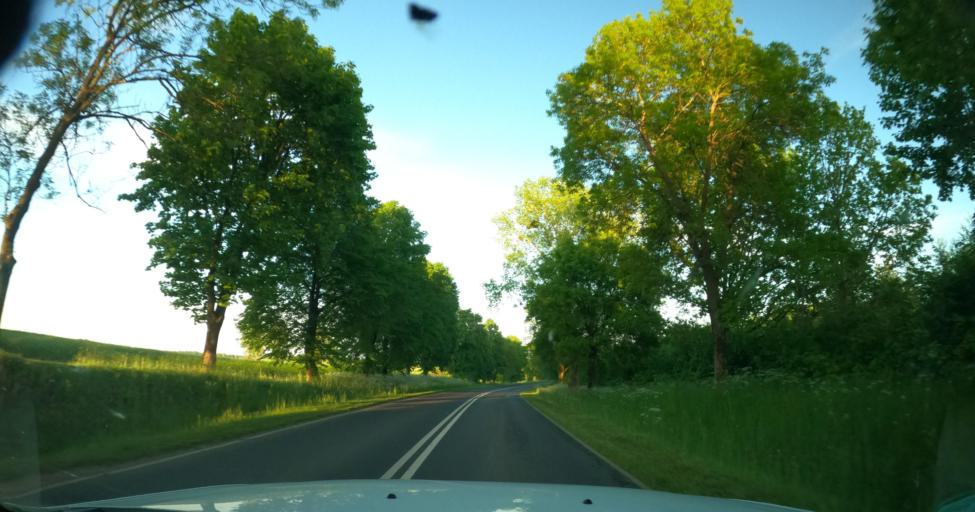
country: PL
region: Warmian-Masurian Voivodeship
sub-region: Powiat lidzbarski
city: Lidzbark Warminski
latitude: 54.1445
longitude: 20.4966
